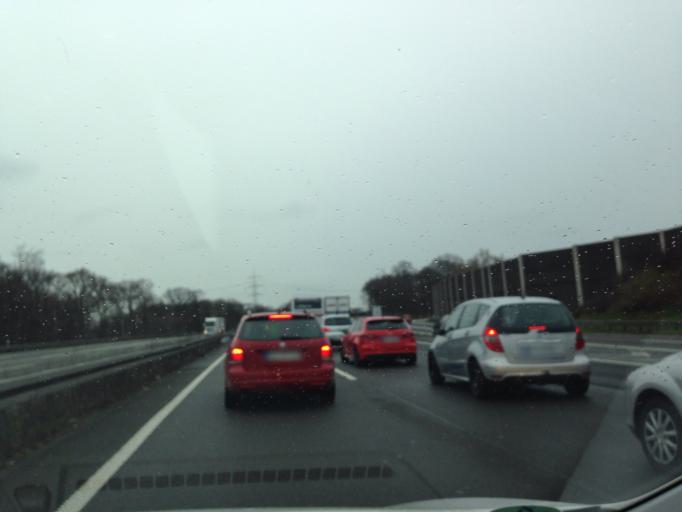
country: DE
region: North Rhine-Westphalia
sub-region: Regierungsbezirk Dusseldorf
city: Meerbusch
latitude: 51.2869
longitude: 6.6355
